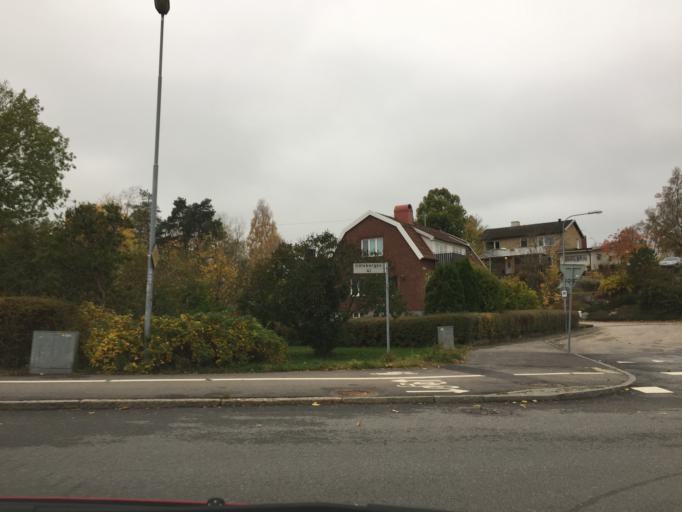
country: SE
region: Vaestra Goetaland
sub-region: Trollhattan
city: Trollhattan
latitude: 58.2690
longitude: 12.2801
